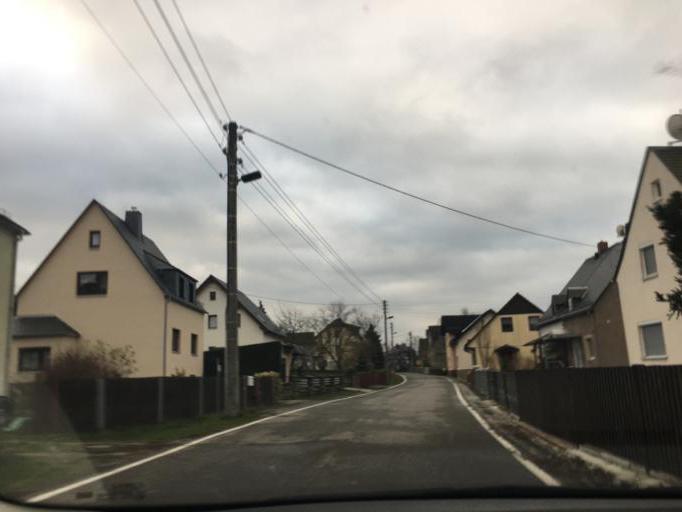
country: DE
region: Saxony
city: Hohenstein-Ernstthal
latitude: 50.8504
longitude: 12.7100
